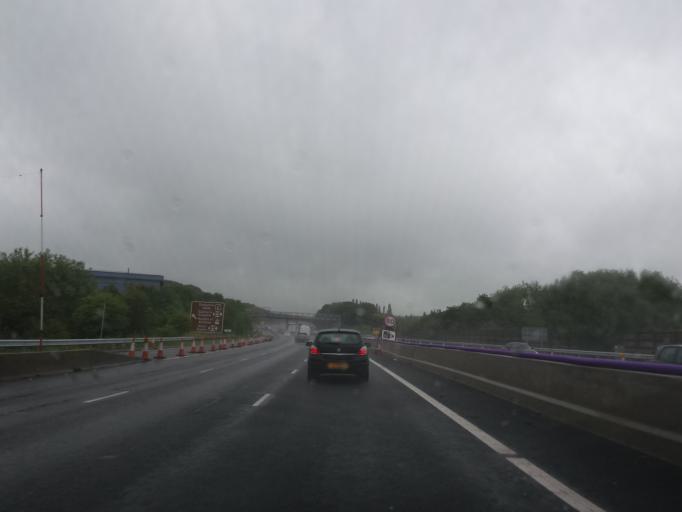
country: GB
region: England
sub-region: Derbyshire
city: Blackwell
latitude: 53.1119
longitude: -1.3321
